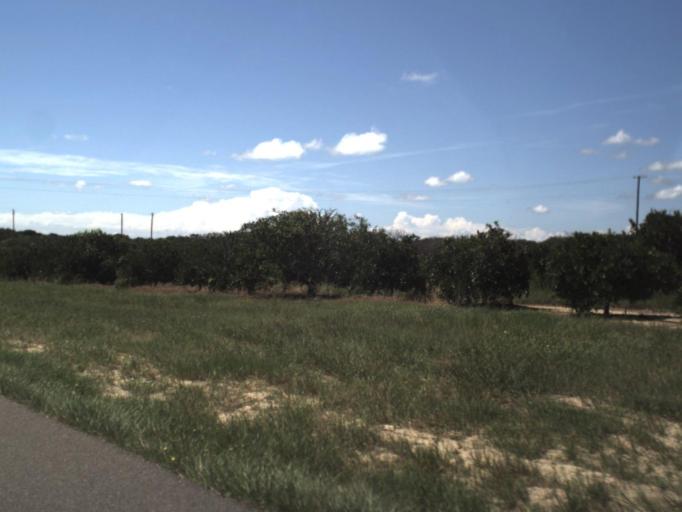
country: US
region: Florida
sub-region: Polk County
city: Crooked Lake Park
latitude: 27.8593
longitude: -81.5731
